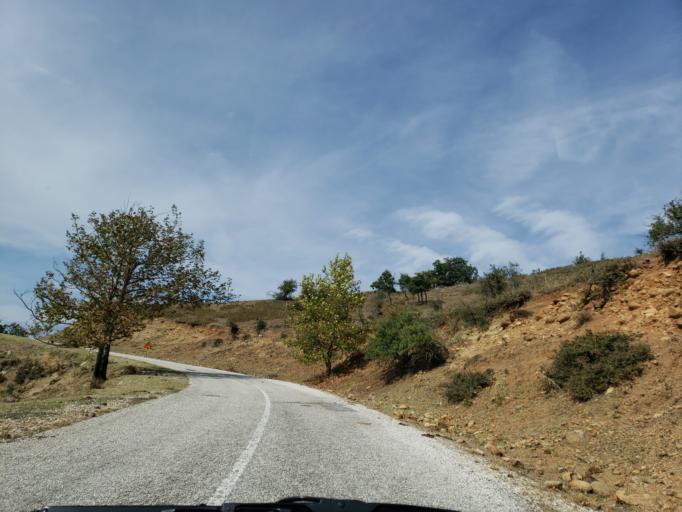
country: GR
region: Thessaly
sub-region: Trikala
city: Kastraki
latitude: 39.7517
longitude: 21.6614
